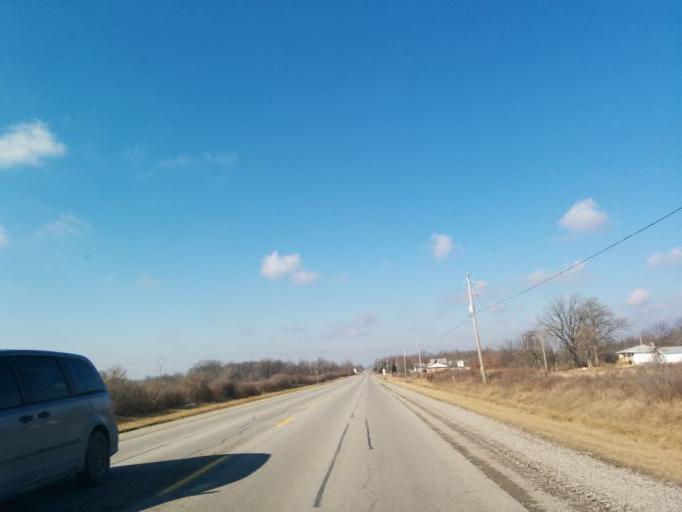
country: CA
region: Ontario
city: Brantford
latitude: 42.9963
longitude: -80.1448
